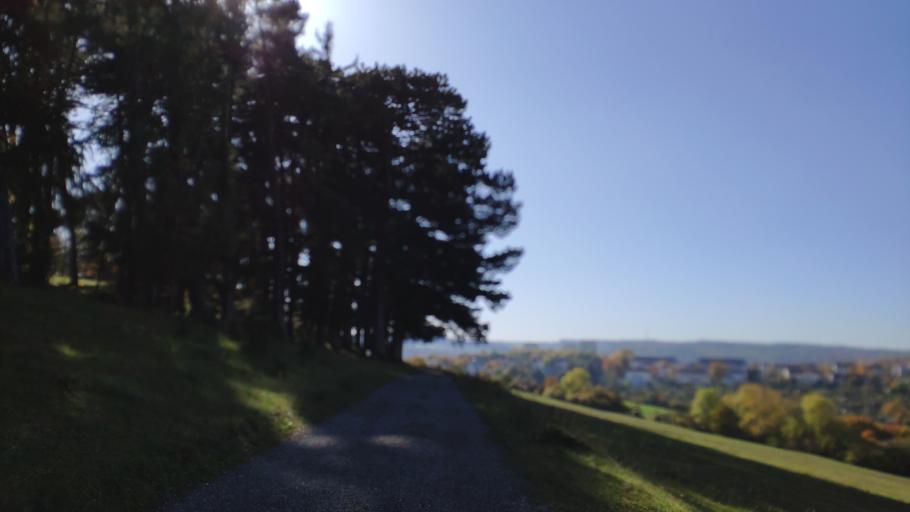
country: DE
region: Baden-Wuerttemberg
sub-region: Tuebingen Region
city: Ulm
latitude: 48.4162
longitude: 9.9763
